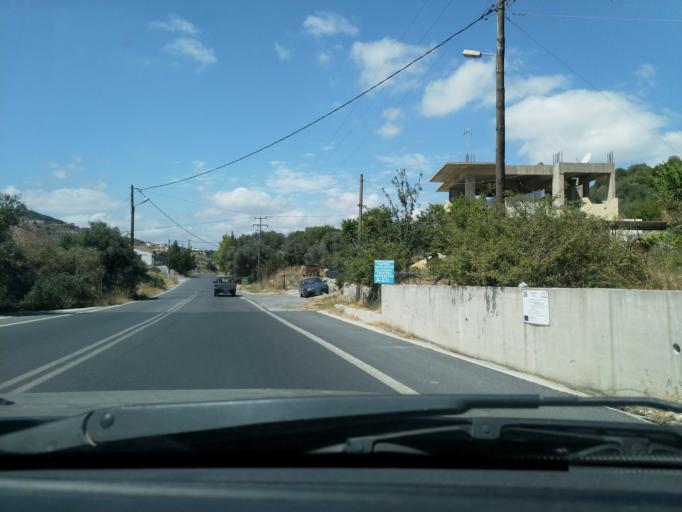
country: GR
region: Crete
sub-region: Nomos Rethymnis
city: Agia Foteini
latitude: 35.2079
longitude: 24.5377
